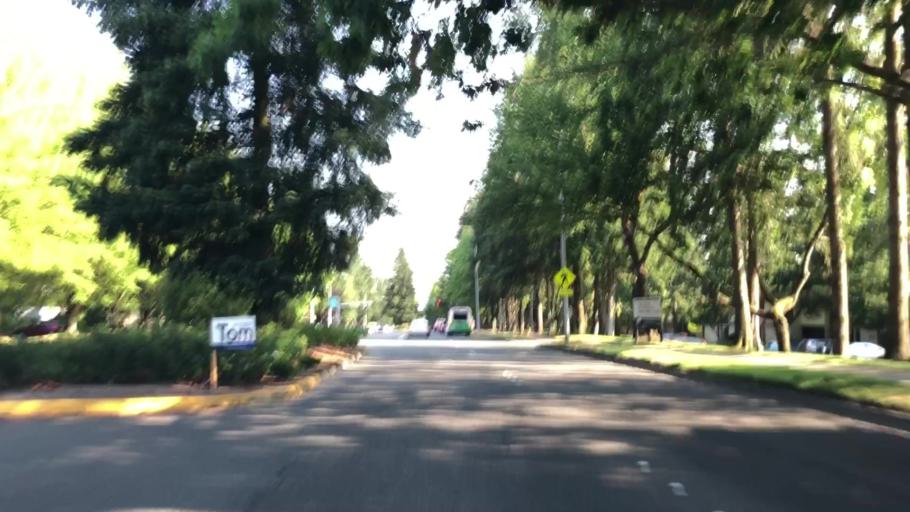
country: US
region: Washington
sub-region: King County
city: Redmond
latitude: 47.6470
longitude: -122.1429
